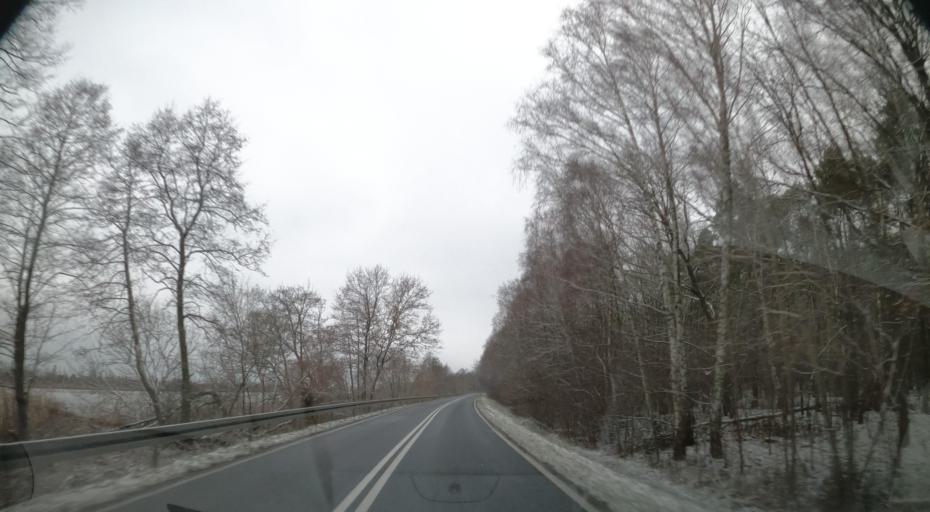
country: PL
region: Masovian Voivodeship
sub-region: Powiat plocki
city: Nowy Duninow
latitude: 52.5750
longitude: 19.5526
